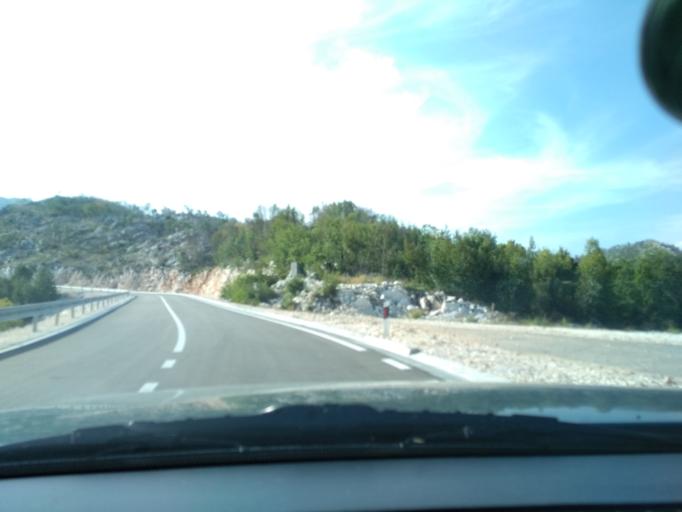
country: ME
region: Cetinje
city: Cetinje
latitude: 42.4251
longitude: 18.8736
